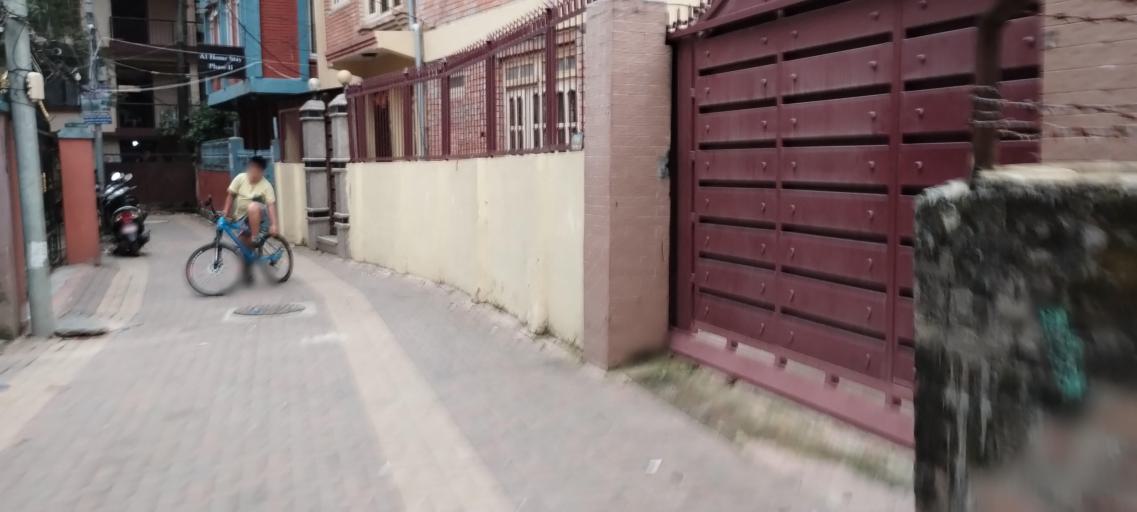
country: NP
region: Central Region
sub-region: Bagmati Zone
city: Kathmandu
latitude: 27.7114
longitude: 85.3102
